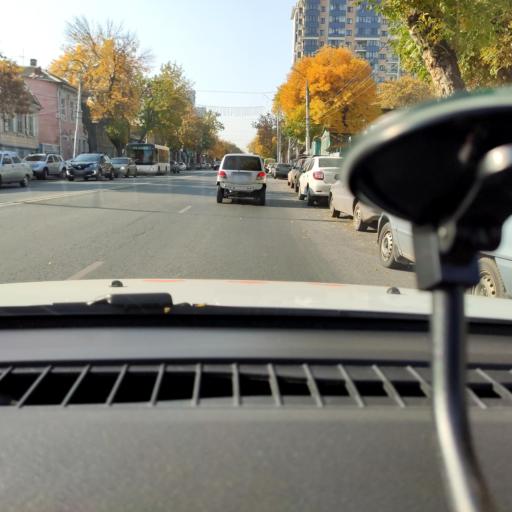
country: RU
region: Samara
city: Samara
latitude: 53.2035
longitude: 50.1197
